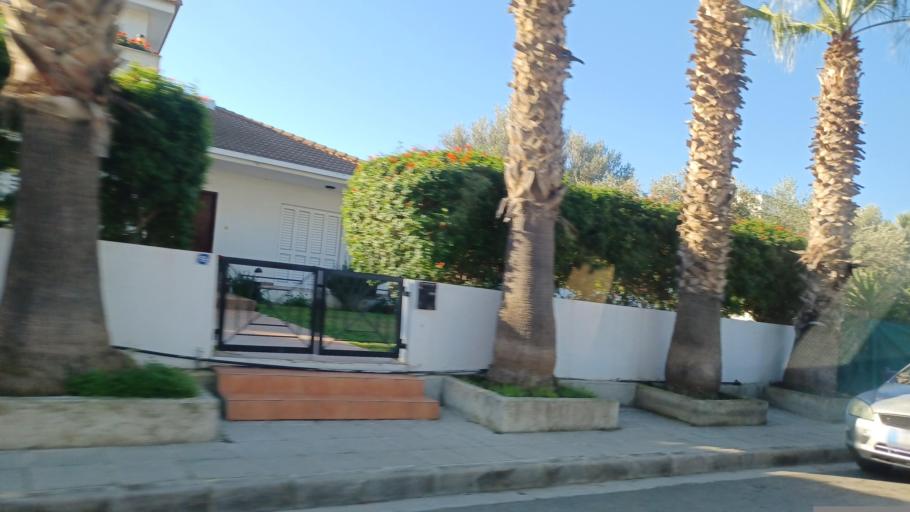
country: CY
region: Lefkosia
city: Nicosia
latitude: 35.1529
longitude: 33.3416
